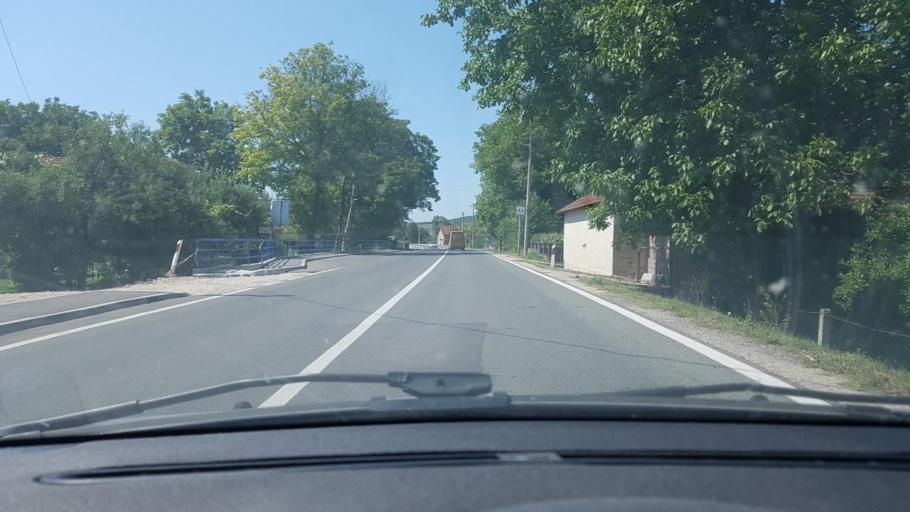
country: BA
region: Federation of Bosnia and Herzegovina
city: Bihac
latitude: 44.7902
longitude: 15.9291
